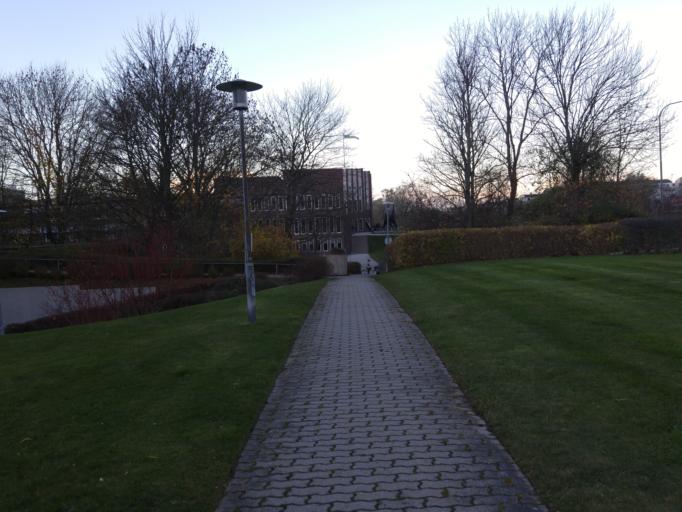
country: SE
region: Skane
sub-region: Lunds Kommun
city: Lund
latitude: 55.7223
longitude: 13.2018
